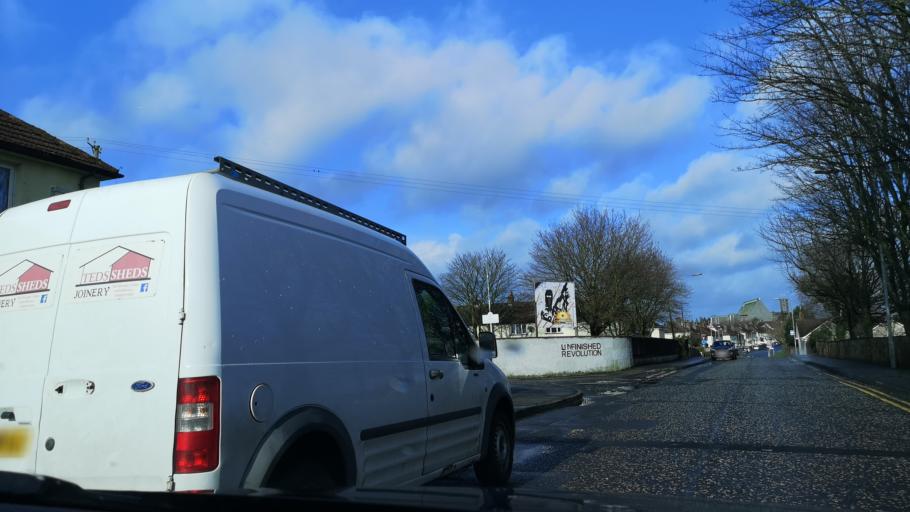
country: GB
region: Northern Ireland
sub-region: Newry and Mourne District
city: Newry
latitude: 54.1810
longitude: -6.3486
